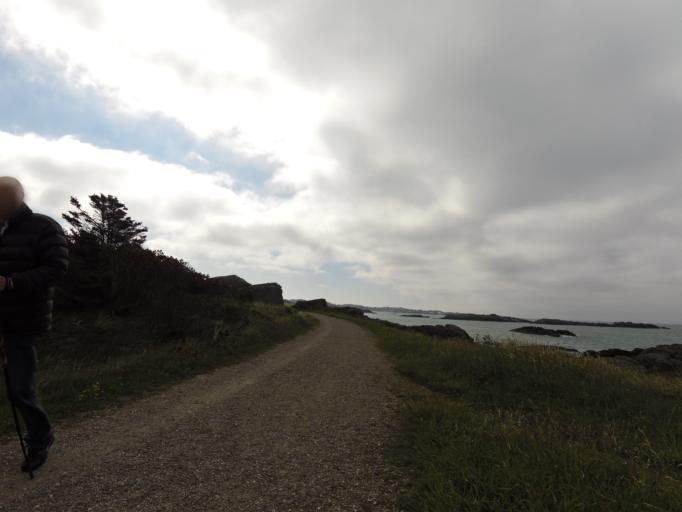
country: NO
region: Rogaland
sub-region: Ha
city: Vigrestad
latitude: 58.5263
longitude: 5.7757
